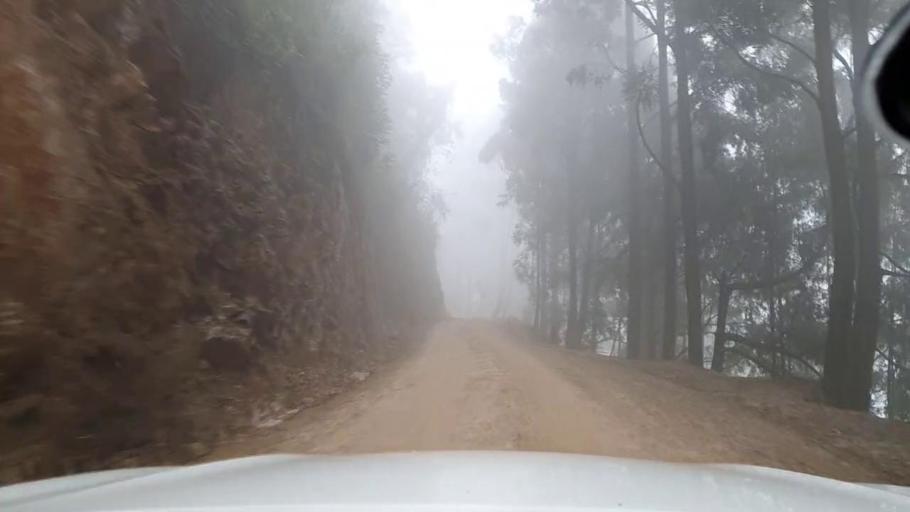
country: BI
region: Cibitoke
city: Cibitoke
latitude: -2.5919
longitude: 29.1916
